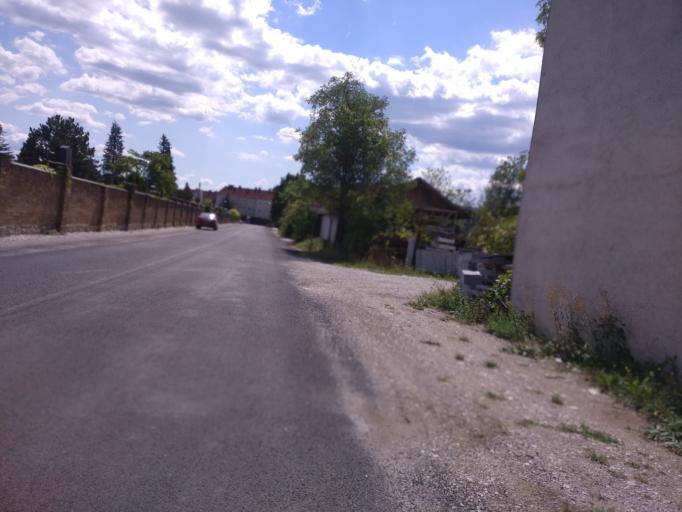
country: AT
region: Lower Austria
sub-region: Politischer Bezirk Neunkirchen
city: Neunkirchen
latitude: 47.7268
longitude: 16.0918
